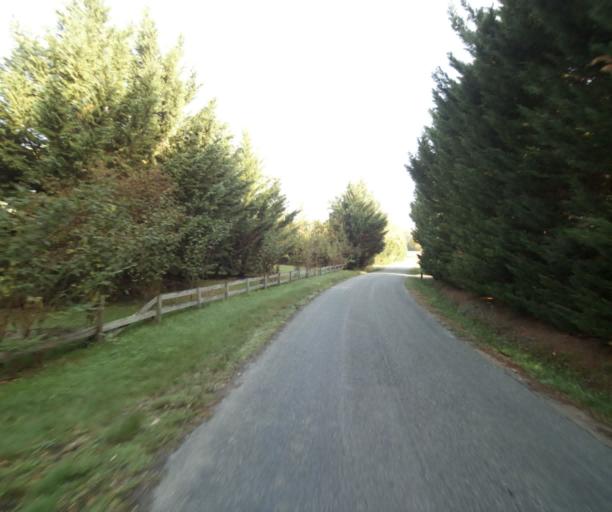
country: FR
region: Midi-Pyrenees
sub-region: Departement de la Haute-Garonne
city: Villemur-sur-Tarn
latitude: 43.9261
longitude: 1.5045
